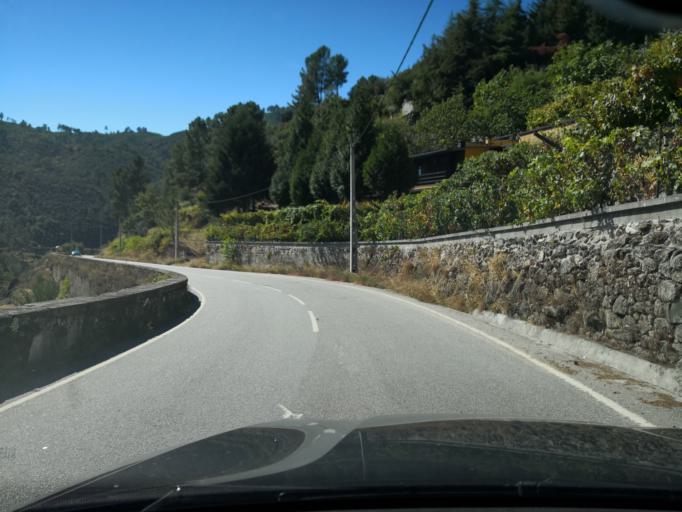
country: PT
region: Vila Real
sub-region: Vila Real
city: Vila Real
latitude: 41.2709
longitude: -7.7790
